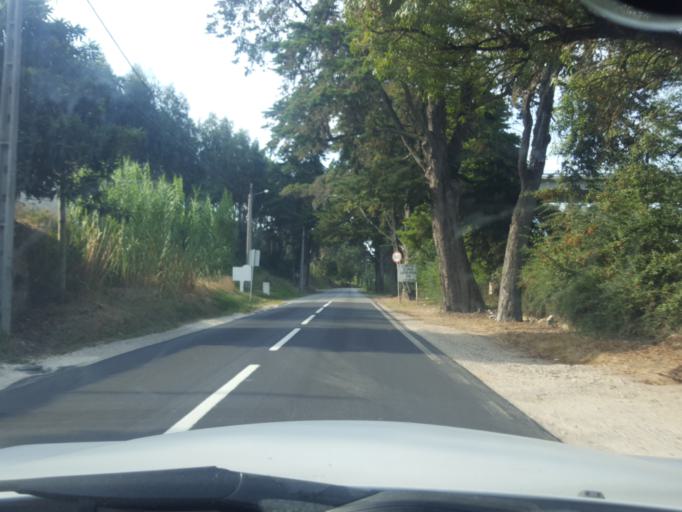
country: PT
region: Leiria
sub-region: Leiria
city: Leiria
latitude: 39.7225
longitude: -8.7948
